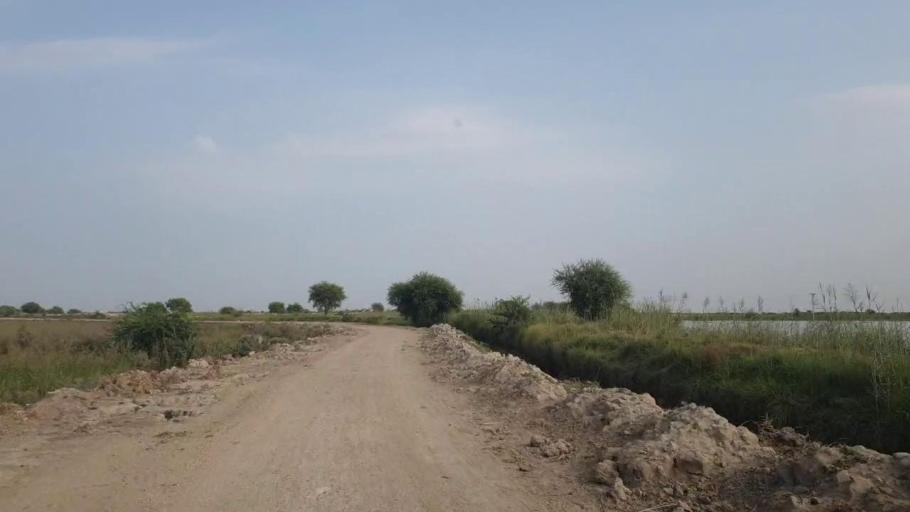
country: PK
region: Sindh
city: Kadhan
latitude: 24.4587
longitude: 68.8073
